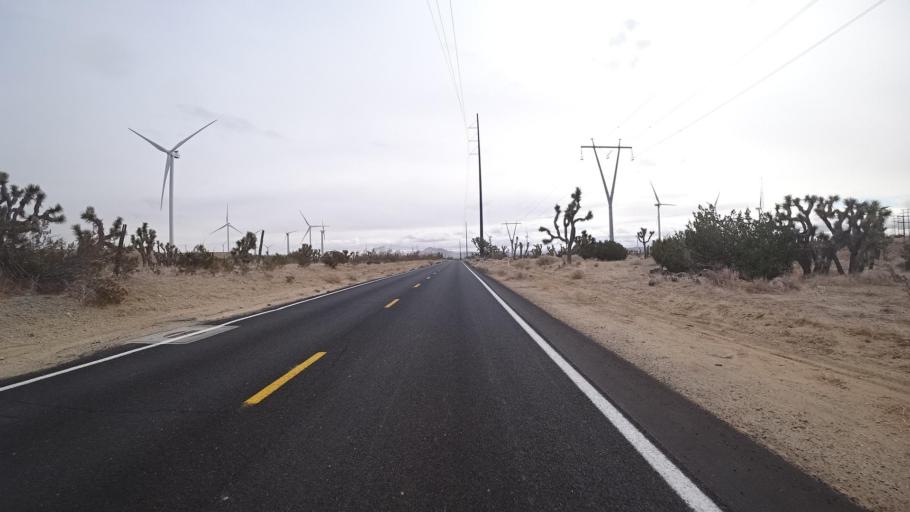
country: US
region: California
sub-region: Kern County
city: Mojave
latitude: 35.0432
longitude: -118.3101
